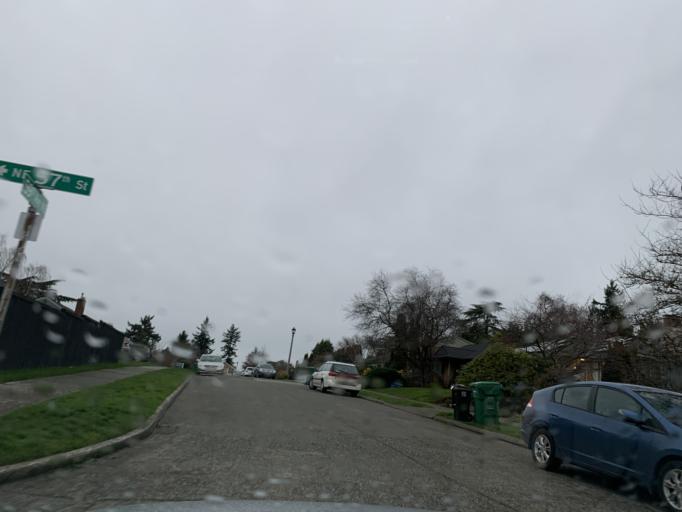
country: US
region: Washington
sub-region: King County
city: Yarrow Point
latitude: 47.6700
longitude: -122.2646
